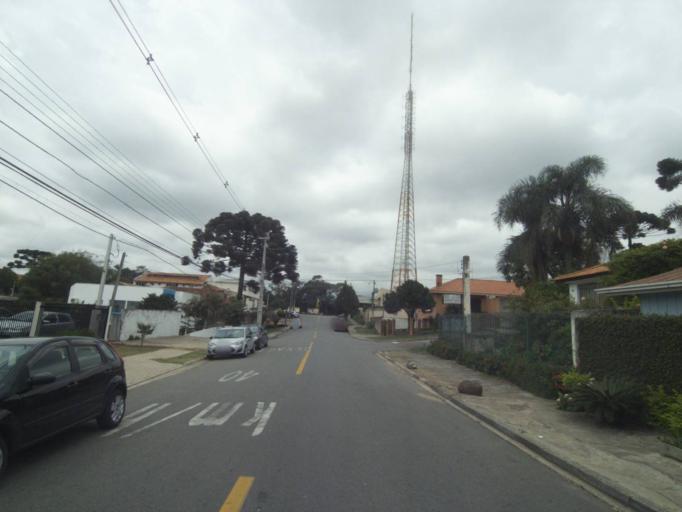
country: BR
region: Parana
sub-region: Curitiba
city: Curitiba
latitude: -25.3950
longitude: -49.2867
